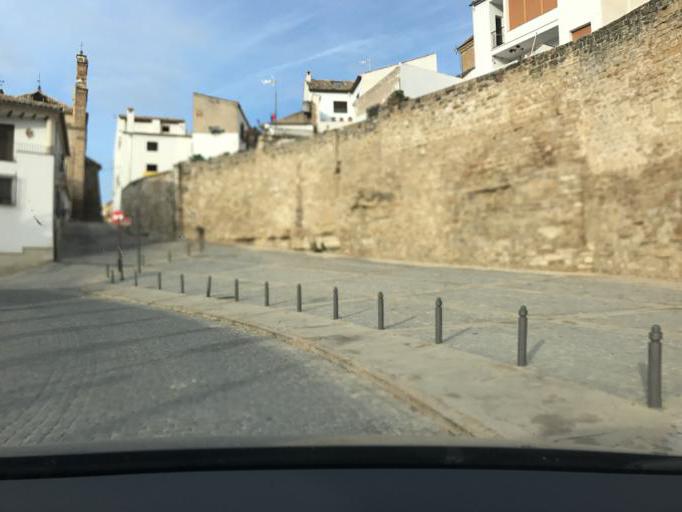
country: ES
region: Andalusia
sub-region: Provincia de Jaen
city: Ubeda
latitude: 38.0069
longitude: -3.3705
